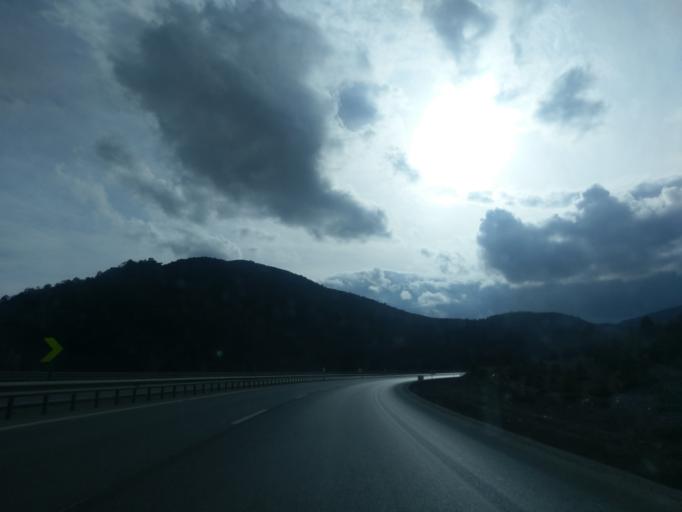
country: TR
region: Kuetahya
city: Sabuncu
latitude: 39.5594
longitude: 30.0763
